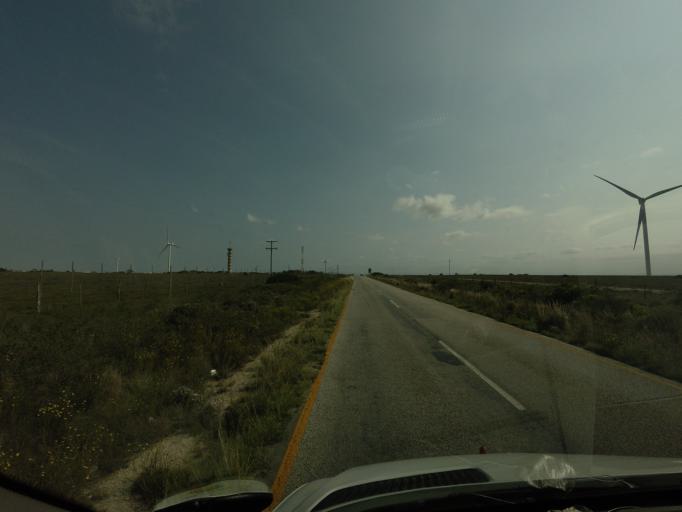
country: ZA
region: Eastern Cape
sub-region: Nelson Mandela Bay Metropolitan Municipality
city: Uitenhage
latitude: -33.6514
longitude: 25.5921
